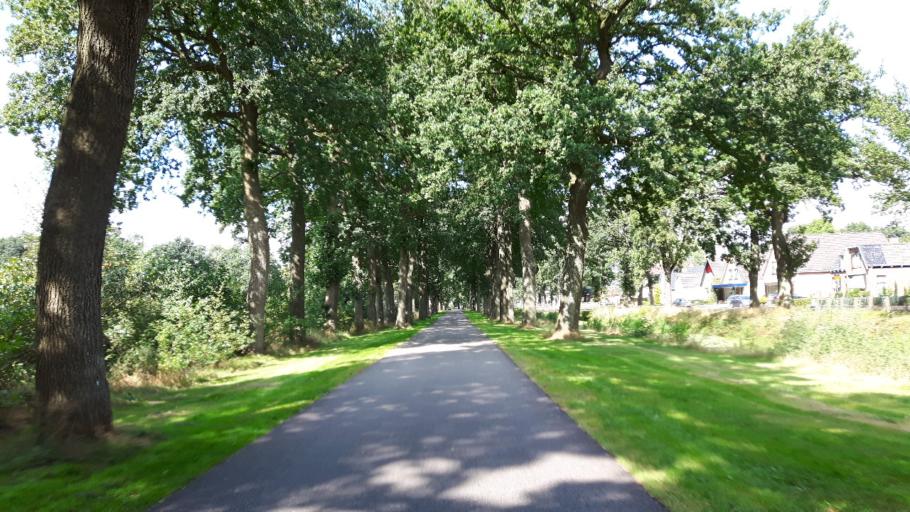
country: NL
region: Friesland
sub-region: Gemeente Smallingerland
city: Drachtstercompagnie
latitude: 53.0776
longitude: 6.2598
